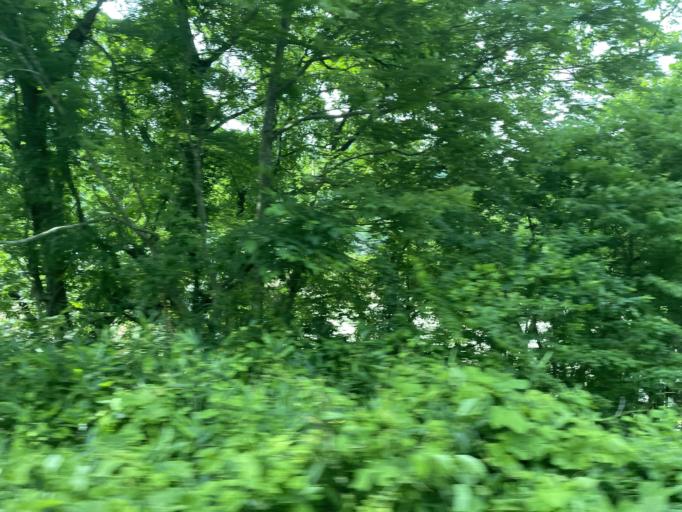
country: JP
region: Fukushima
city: Kitakata
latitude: 37.6051
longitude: 139.6888
